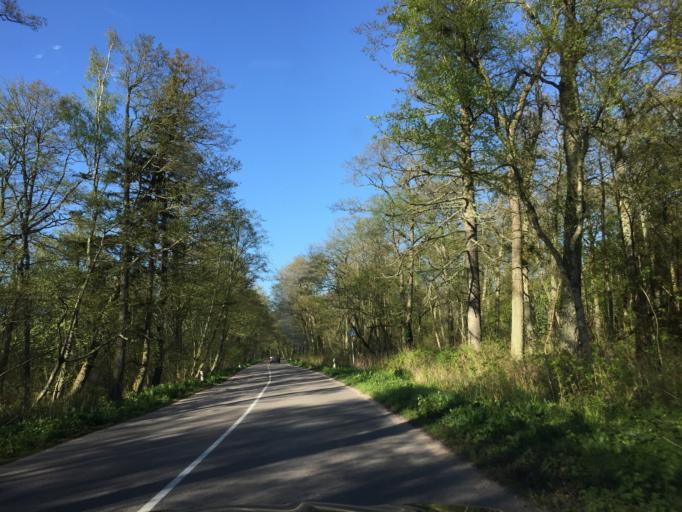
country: LT
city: Nida
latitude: 55.1974
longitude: 20.8666
